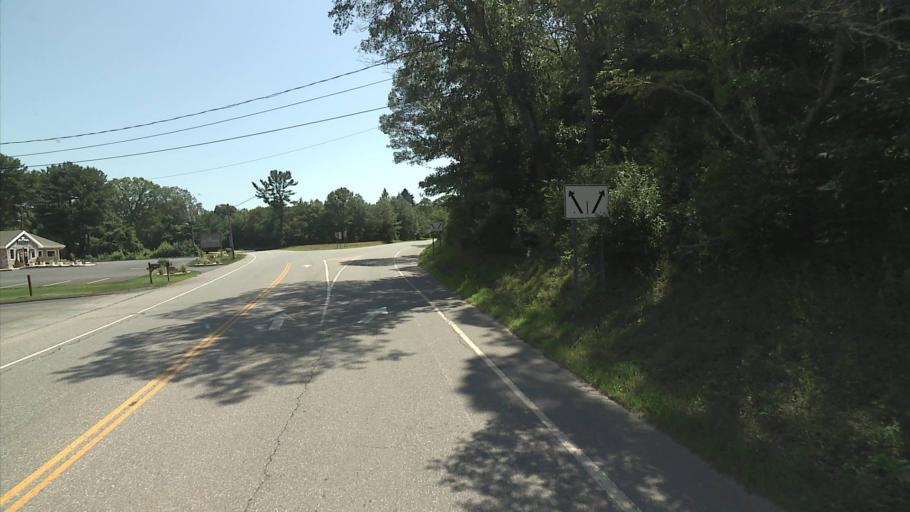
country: US
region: Connecticut
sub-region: Middlesex County
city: Essex Village
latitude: 41.3260
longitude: -72.3780
